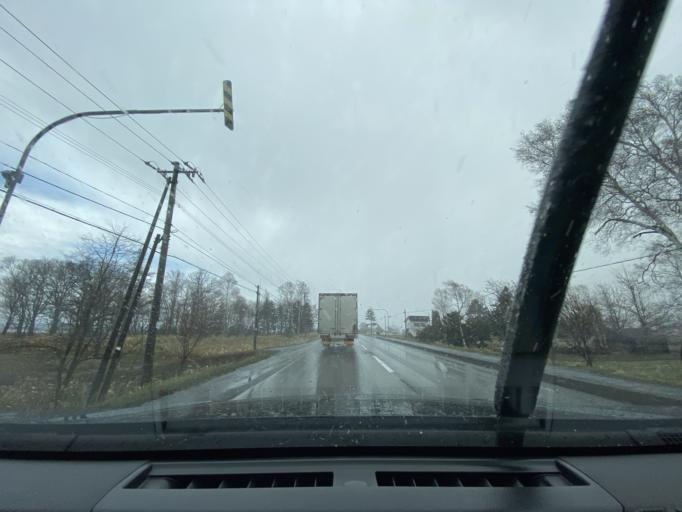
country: JP
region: Hokkaido
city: Fukagawa
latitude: 43.6544
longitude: 141.9775
